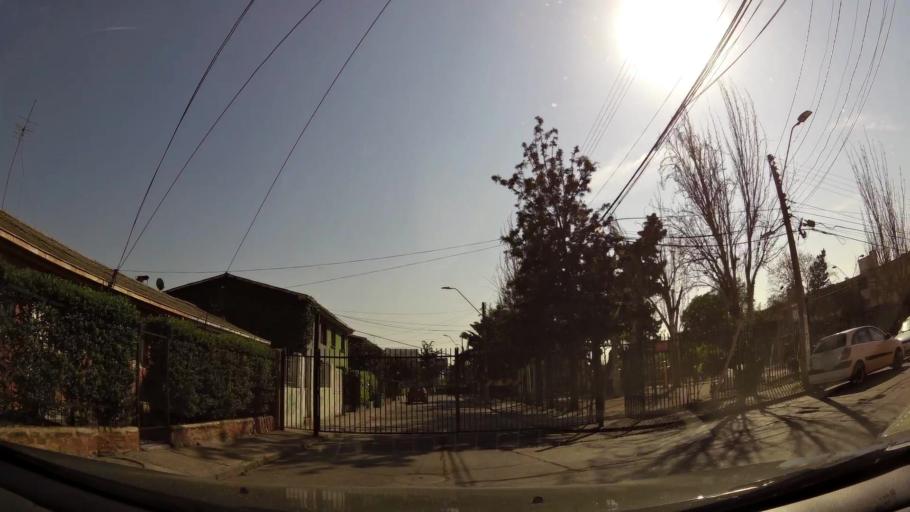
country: CL
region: Santiago Metropolitan
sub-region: Provincia de Maipo
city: San Bernardo
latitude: -33.5984
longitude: -70.7072
